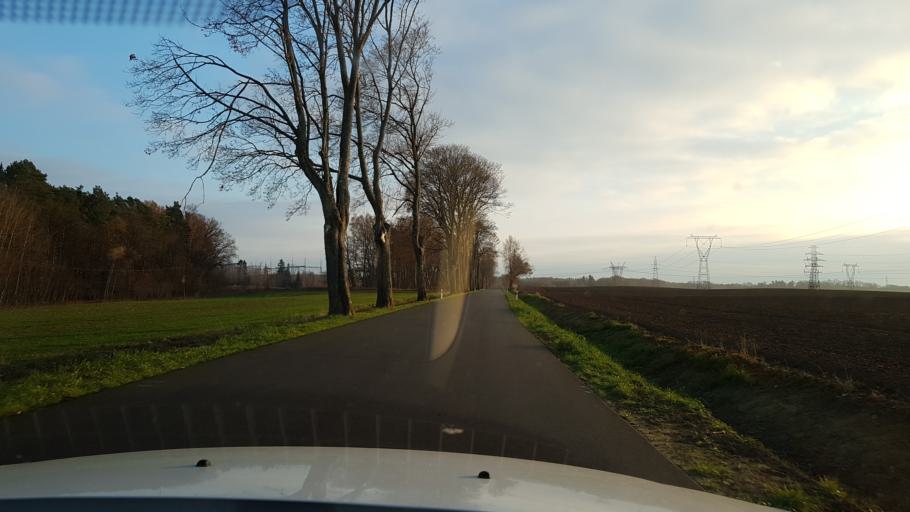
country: PL
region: West Pomeranian Voivodeship
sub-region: Koszalin
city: Koszalin
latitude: 54.1320
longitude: 16.0863
